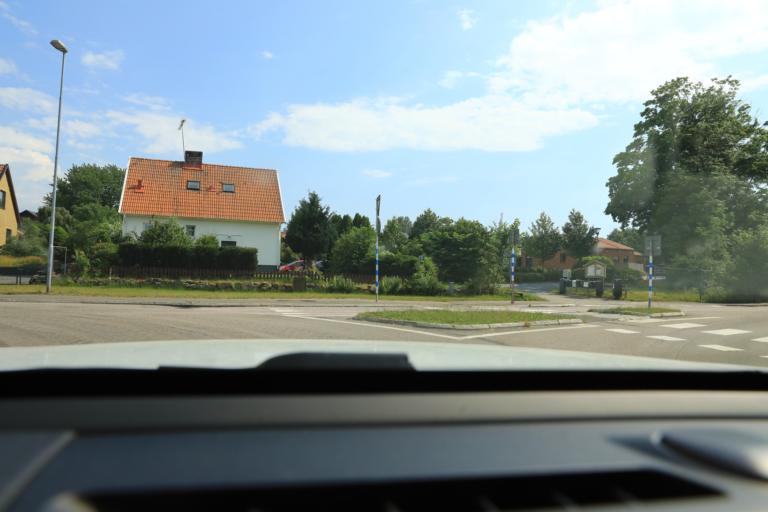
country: SE
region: Halland
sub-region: Varbergs Kommun
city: Varberg
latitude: 57.1596
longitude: 12.3129
